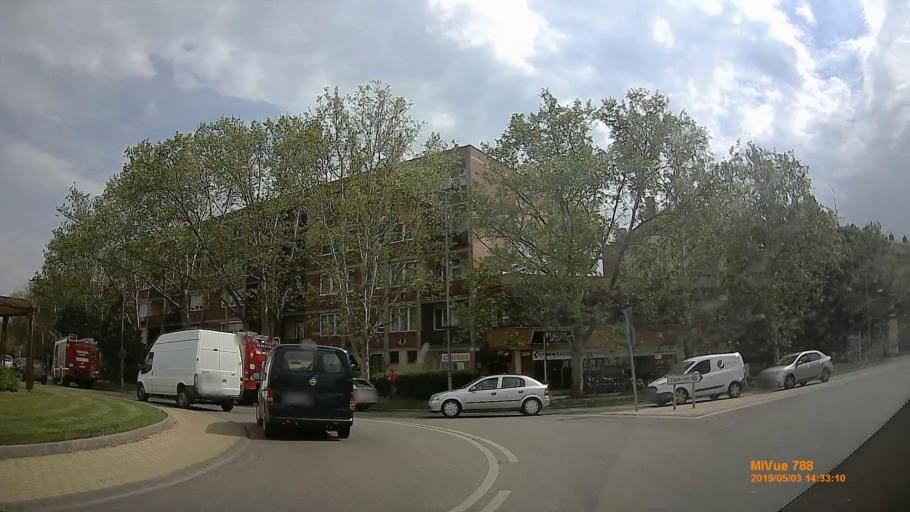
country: HU
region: Jasz-Nagykun-Szolnok
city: Szolnok
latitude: 47.1807
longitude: 20.1982
